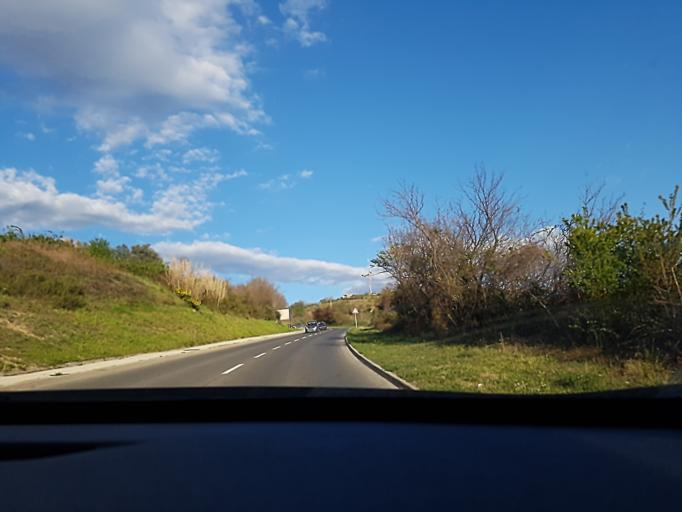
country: SI
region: Izola-Isola
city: Izola
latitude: 45.5429
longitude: 13.6877
